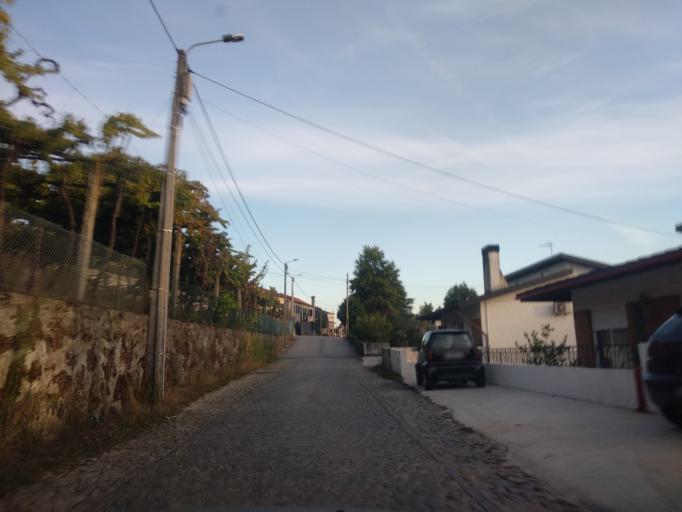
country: PT
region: Braga
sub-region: Vila Nova de Famalicao
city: Vila Nova de Famalicao
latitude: 41.4045
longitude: -8.5106
